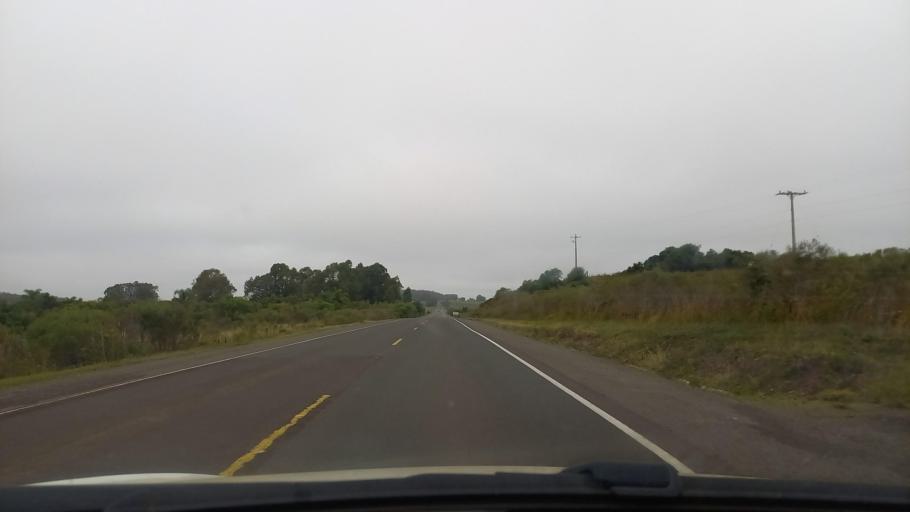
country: BR
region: Rio Grande do Sul
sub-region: Rosario Do Sul
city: Rosario do Sul
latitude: -30.3096
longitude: -54.9955
